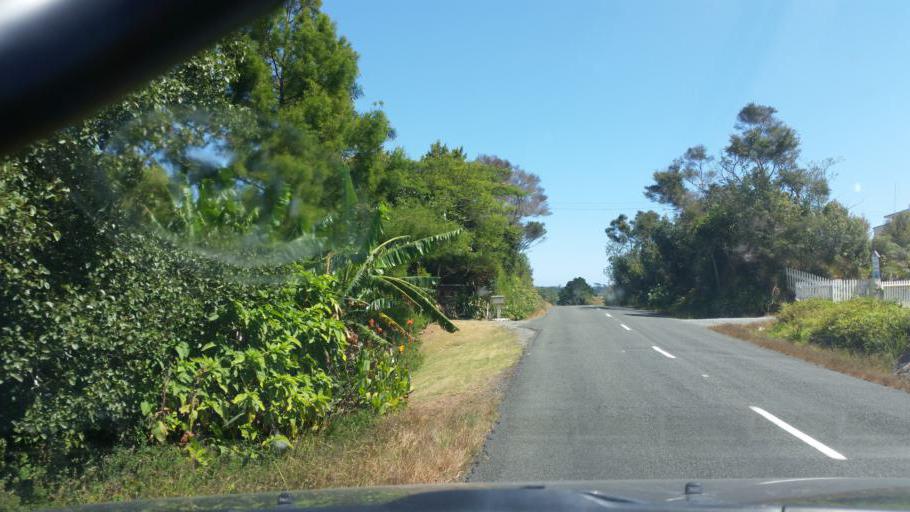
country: NZ
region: Northland
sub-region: Kaipara District
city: Dargaville
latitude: -36.0124
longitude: 173.9367
